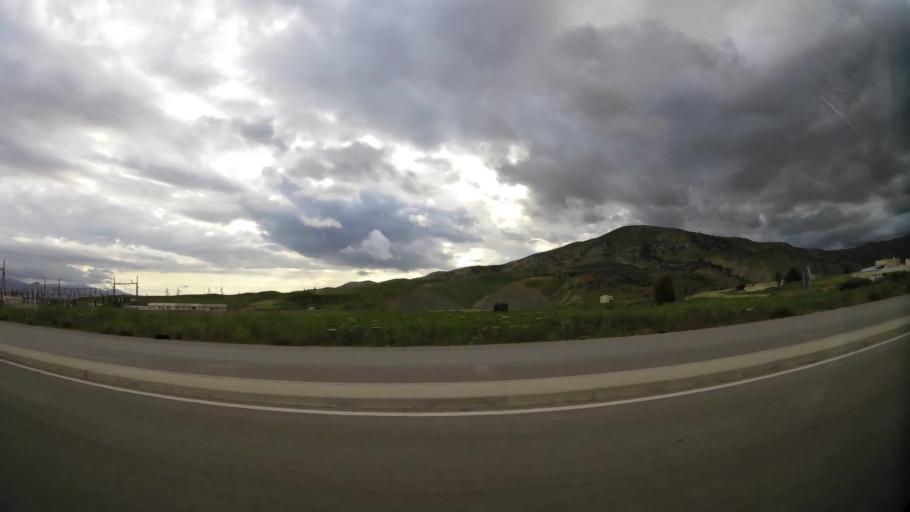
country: MA
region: Taza-Al Hoceima-Taounate
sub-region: Taza
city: Taza
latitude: 34.2701
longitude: -3.9566
